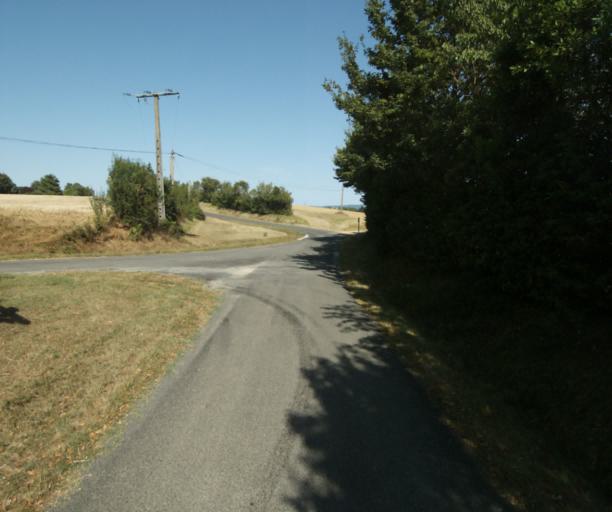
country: FR
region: Midi-Pyrenees
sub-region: Departement de la Haute-Garonne
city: Saint-Felix-Lauragais
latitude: 43.4269
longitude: 1.8565
